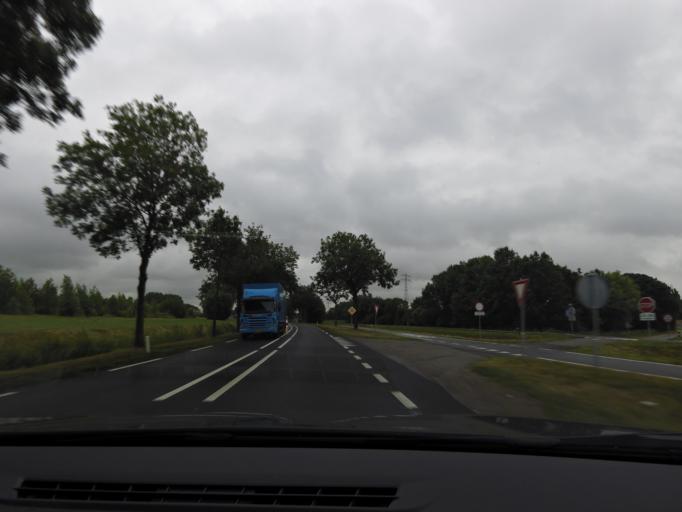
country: NL
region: South Holland
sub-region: Gemeente Maassluis
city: Maassluis
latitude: 51.8713
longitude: 4.2212
